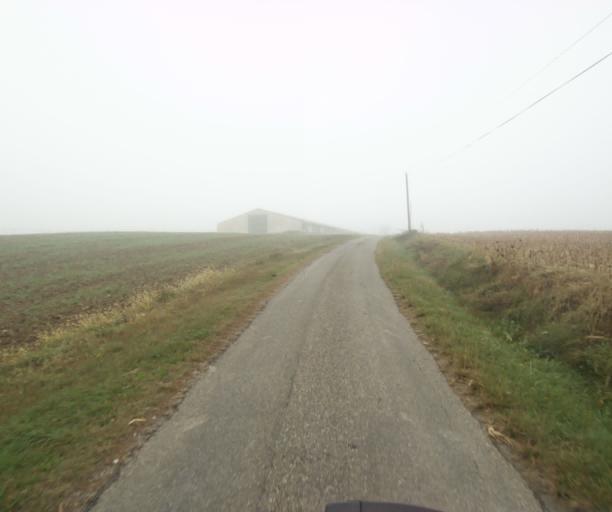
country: FR
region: Midi-Pyrenees
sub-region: Departement du Tarn-et-Garonne
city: Nohic
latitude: 43.9058
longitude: 1.4753
